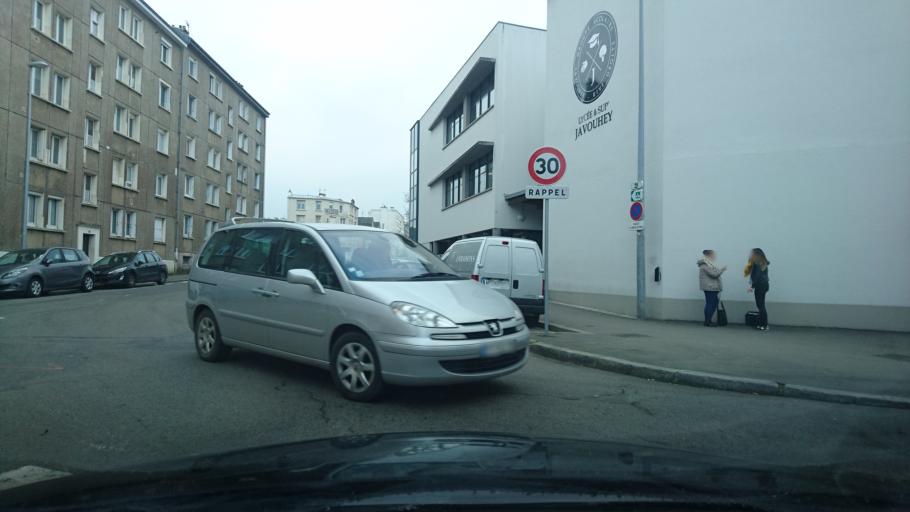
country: FR
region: Brittany
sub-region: Departement du Finistere
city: Brest
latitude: 48.3823
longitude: -4.5020
